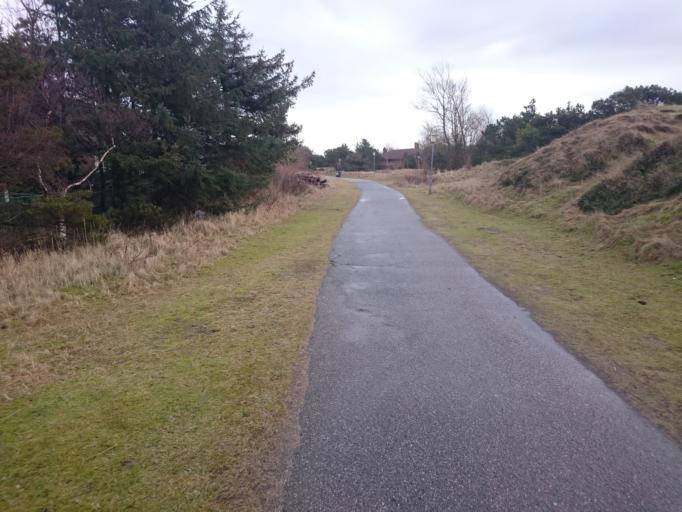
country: DK
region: South Denmark
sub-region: Fano Kommune
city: Nordby
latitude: 55.4414
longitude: 8.3903
